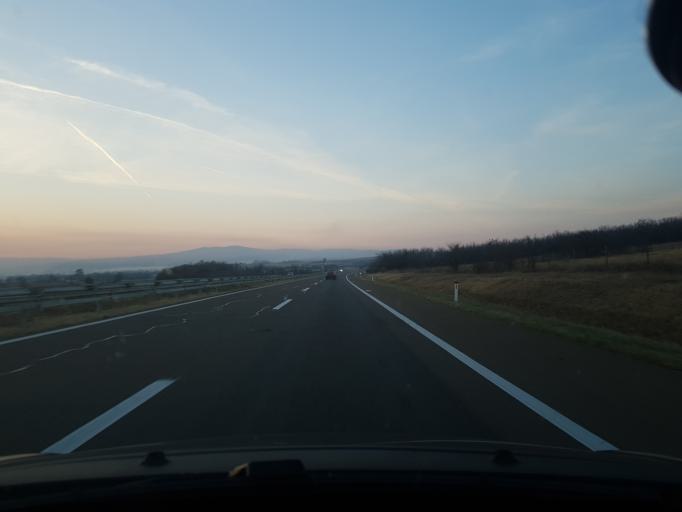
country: RS
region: Central Serbia
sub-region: Nisavski Okrug
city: Razanj
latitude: 43.6140
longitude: 21.5982
